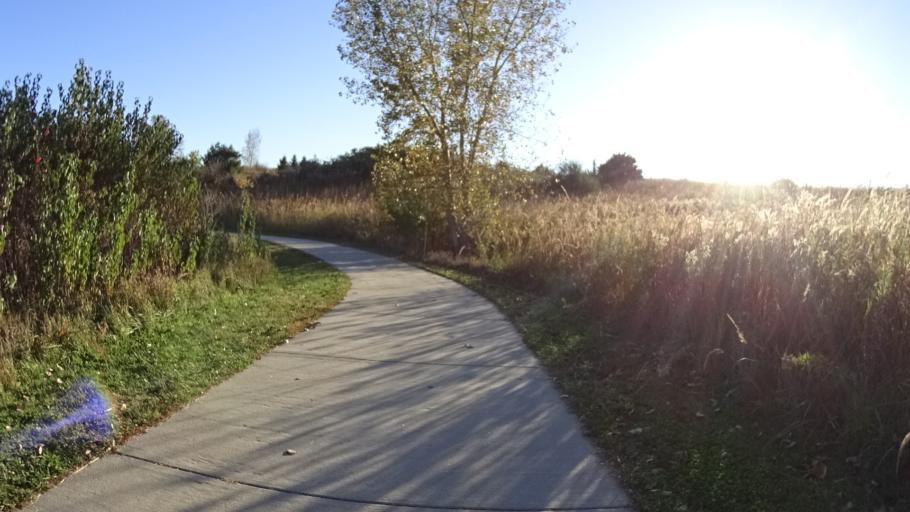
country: US
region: Nebraska
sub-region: Sarpy County
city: Papillion
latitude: 41.1404
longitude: -96.0717
